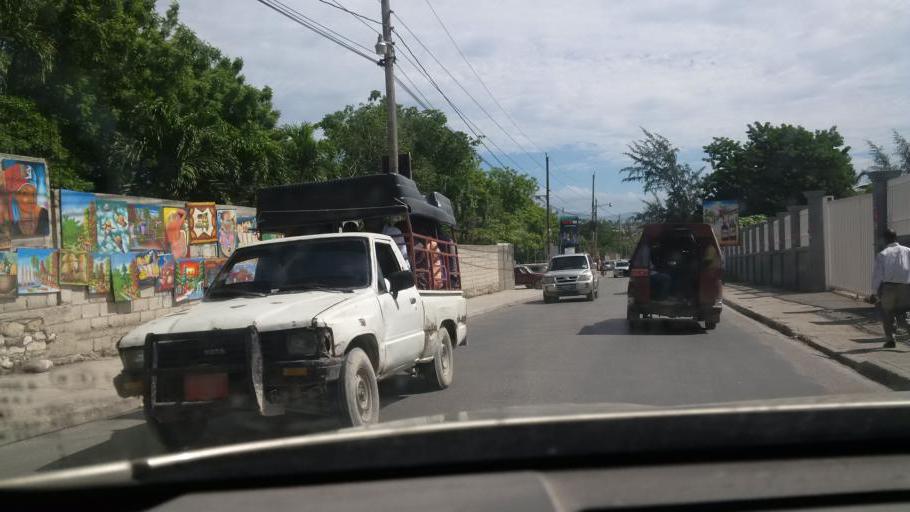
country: HT
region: Ouest
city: Delmas 73
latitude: 18.5532
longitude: -72.3023
